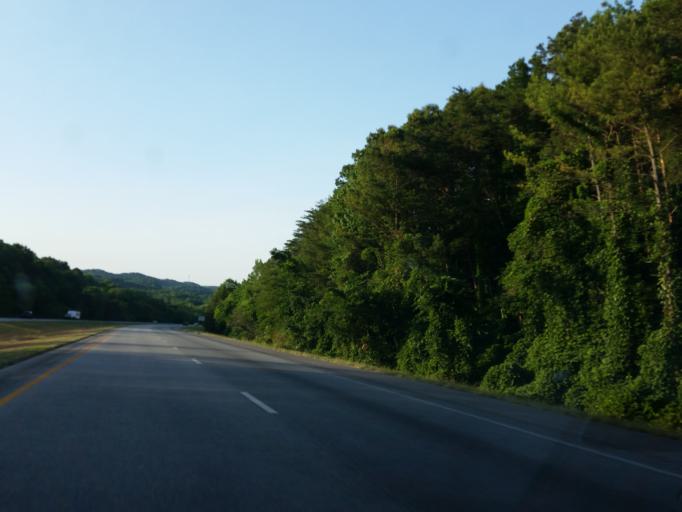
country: US
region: Georgia
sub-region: Dade County
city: Trenton
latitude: 34.8041
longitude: -85.5495
